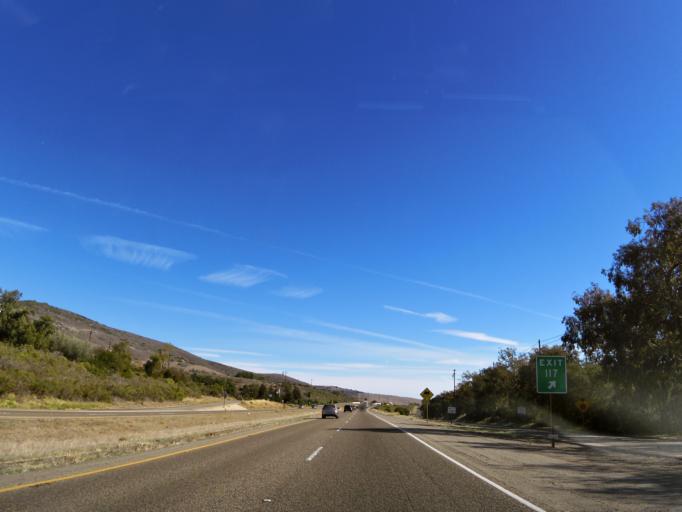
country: US
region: California
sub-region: Santa Barbara County
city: Santa Ynez
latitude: 34.4634
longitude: -120.0272
